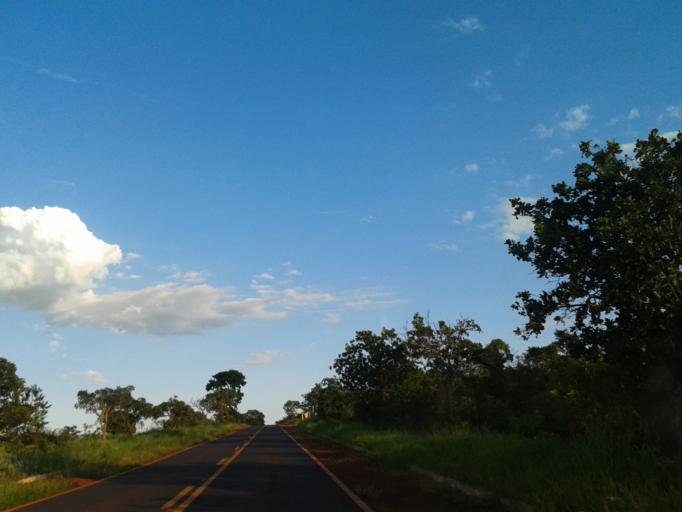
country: BR
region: Minas Gerais
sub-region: Ituiutaba
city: Ituiutaba
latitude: -18.8841
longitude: -49.4613
